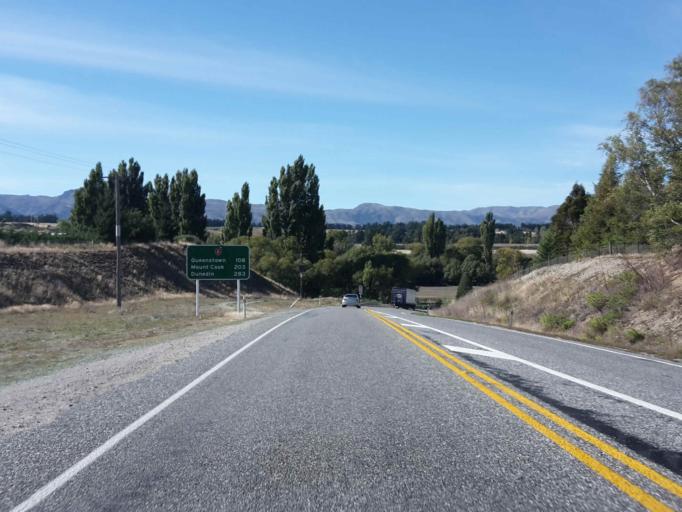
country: NZ
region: Otago
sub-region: Queenstown-Lakes District
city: Wanaka
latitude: -44.6968
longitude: 169.1725
